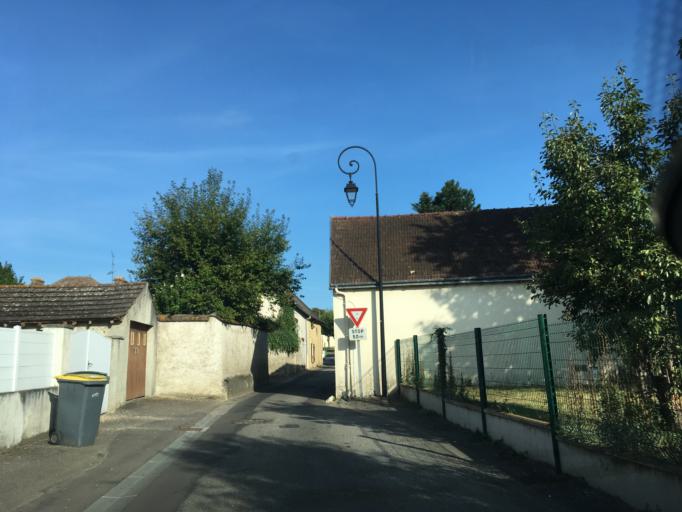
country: FR
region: Haute-Normandie
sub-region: Departement de l'Eure
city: Gasny
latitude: 49.0903
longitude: 1.6026
